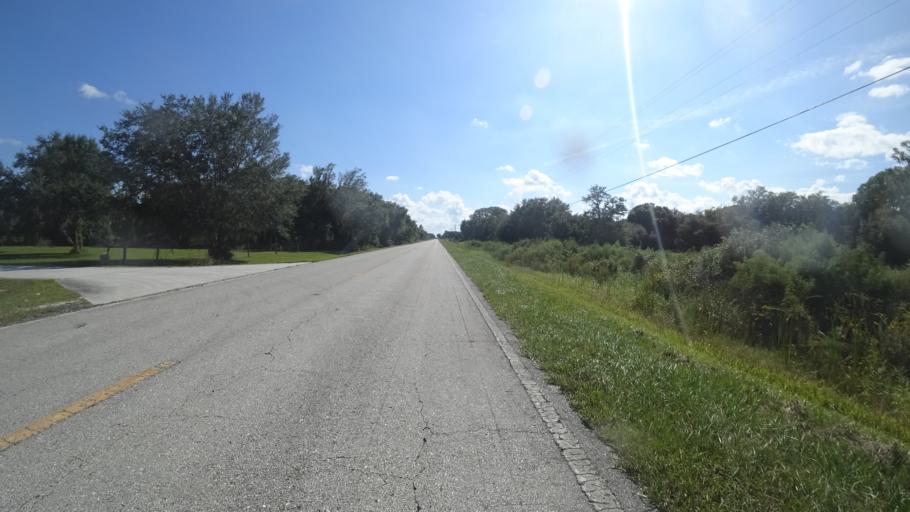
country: US
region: Florida
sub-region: Sarasota County
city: The Meadows
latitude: 27.4550
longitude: -82.3033
